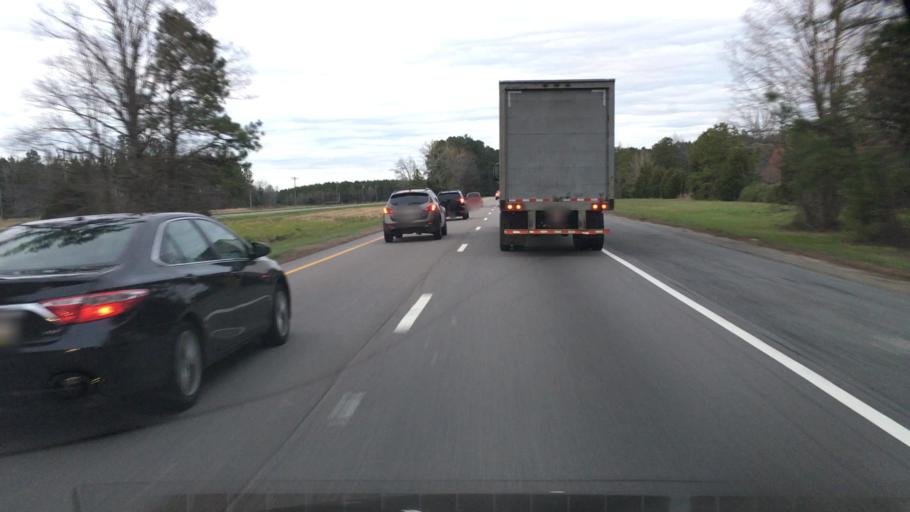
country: US
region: Virginia
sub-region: Sussex County
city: Sussex
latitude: 36.8395
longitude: -77.4416
